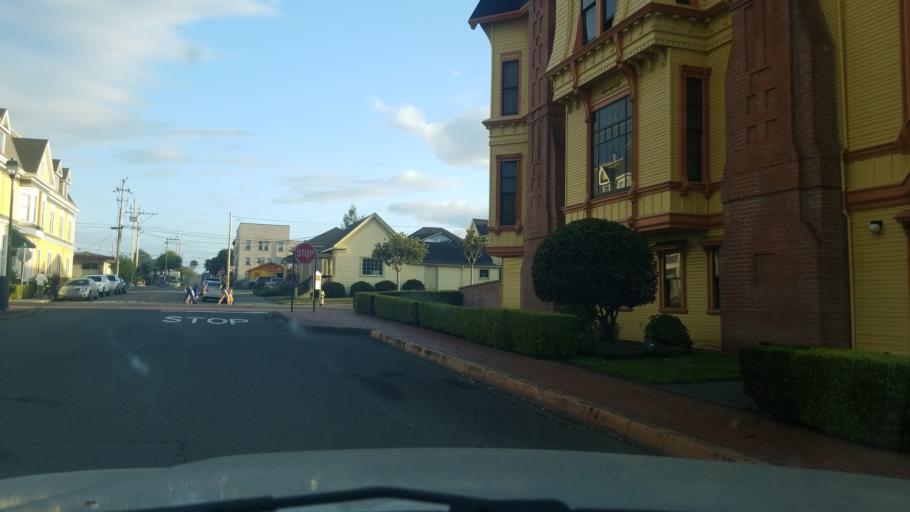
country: US
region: California
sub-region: Humboldt County
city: Eureka
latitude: 40.8048
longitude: -124.1599
